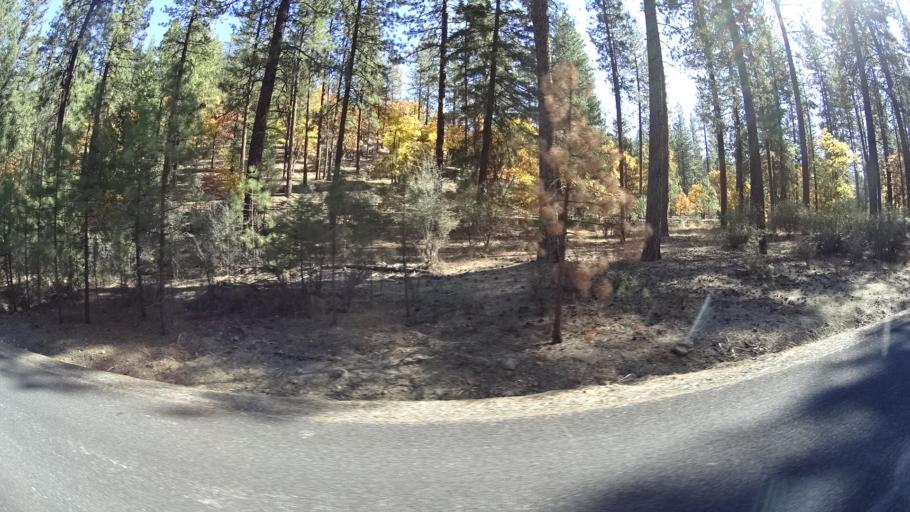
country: US
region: California
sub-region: Siskiyou County
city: Yreka
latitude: 41.6415
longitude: -122.8725
